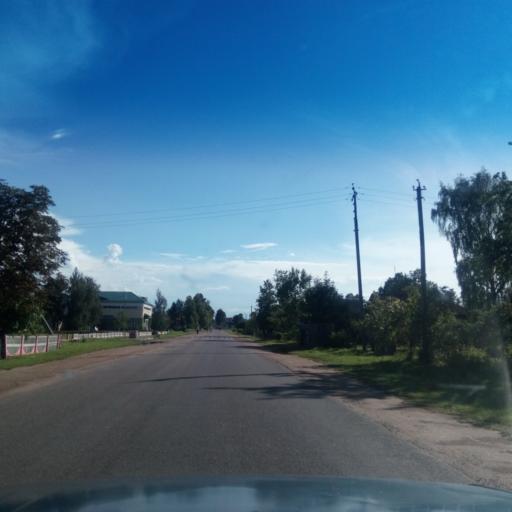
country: BY
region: Vitebsk
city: Dzisna
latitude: 55.6720
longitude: 28.3318
